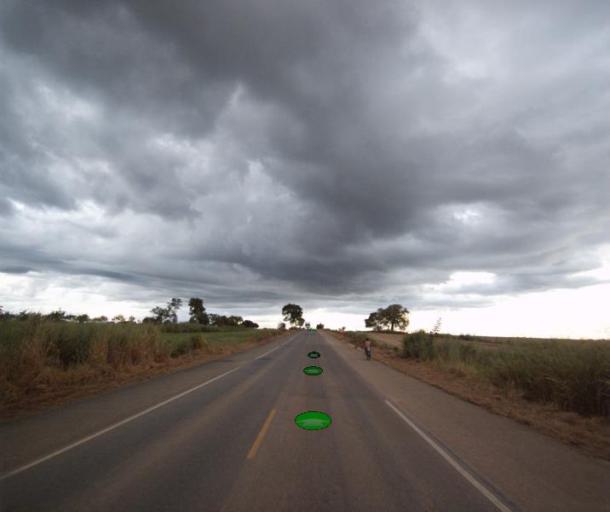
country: BR
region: Goias
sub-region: Uruacu
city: Uruacu
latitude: -14.7012
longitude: -49.2191
